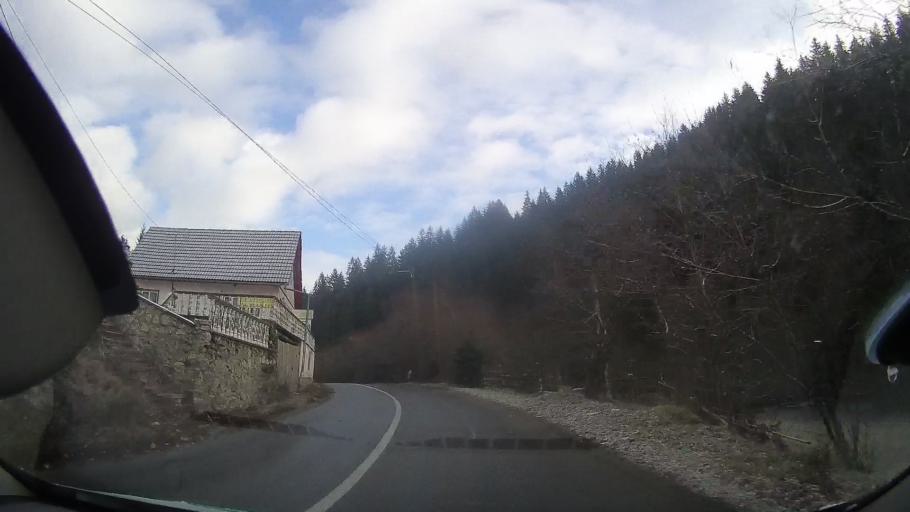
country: RO
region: Alba
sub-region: Comuna Albac
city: Albac
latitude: 46.4543
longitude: 22.9735
